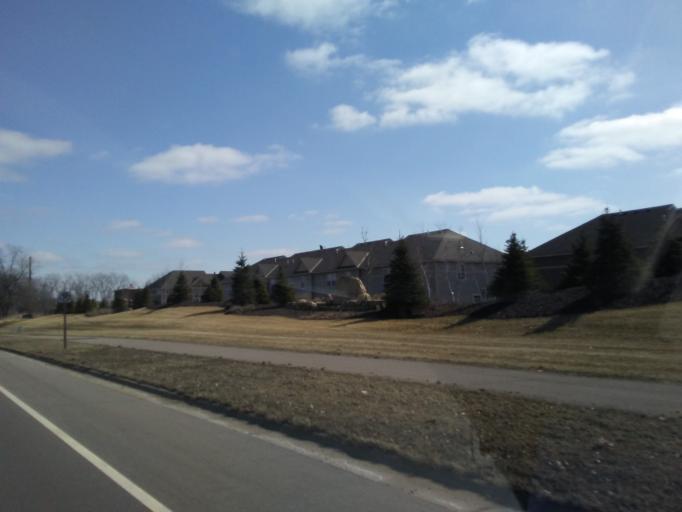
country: US
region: Minnesota
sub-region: Dakota County
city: Eagan
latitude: 44.8335
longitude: -93.1405
